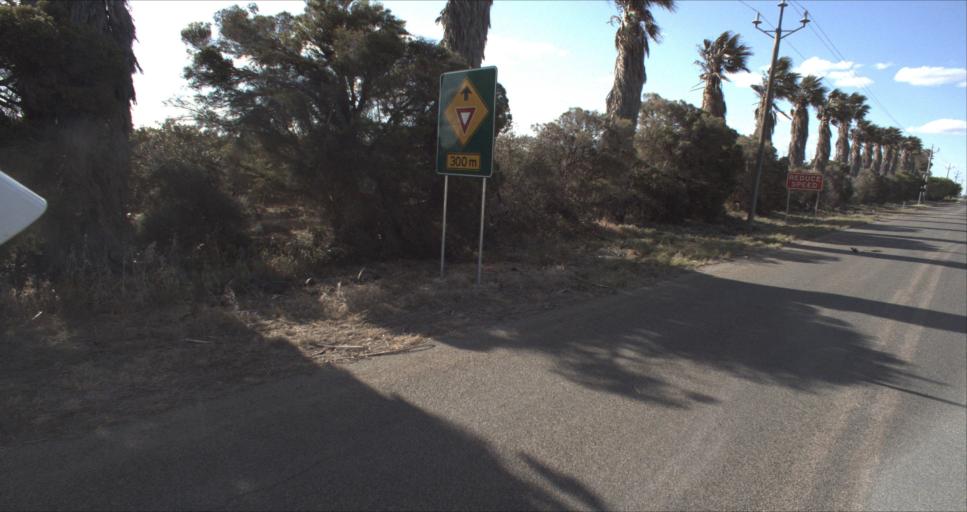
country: AU
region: New South Wales
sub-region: Leeton
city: Leeton
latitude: -34.5227
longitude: 146.2830
